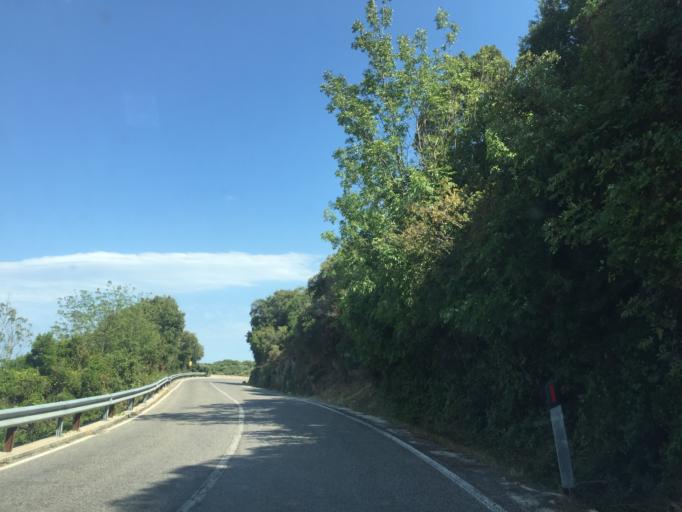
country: IT
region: Sardinia
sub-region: Provincia di Olbia-Tempio
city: Aggius
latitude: 40.9242
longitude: 9.0639
